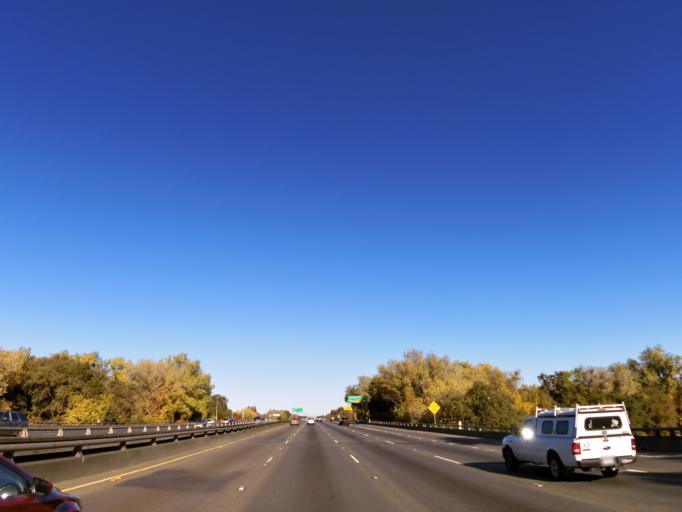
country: US
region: California
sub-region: Sacramento County
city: Sacramento
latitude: 38.6038
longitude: -121.5065
